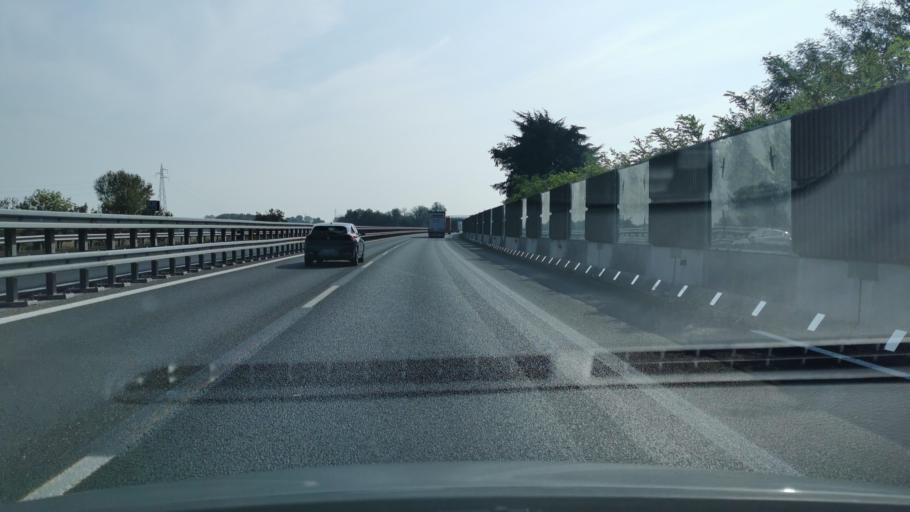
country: IT
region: Lombardy
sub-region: Provincia di Pavia
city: Zerbo
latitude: 45.0844
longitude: 9.3914
